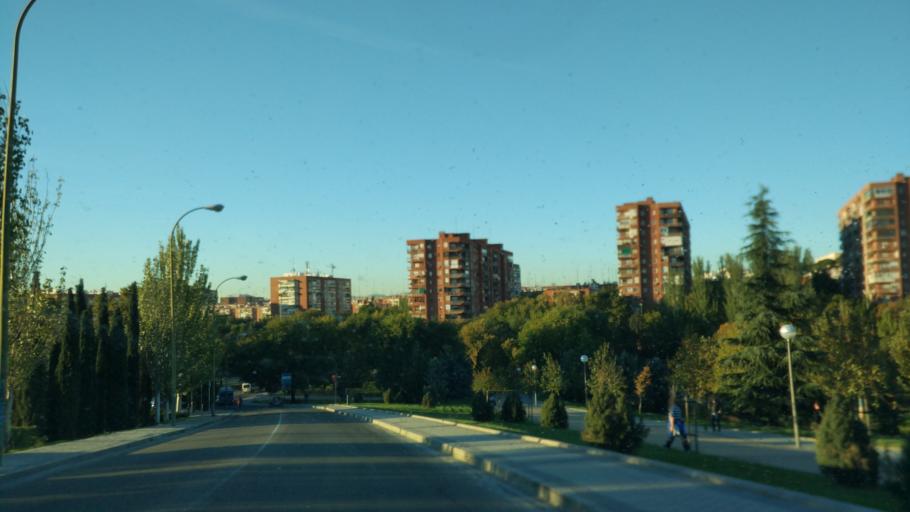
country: ES
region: Madrid
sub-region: Provincia de Madrid
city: Tetuan de las Victorias
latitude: 40.4694
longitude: -3.7101
